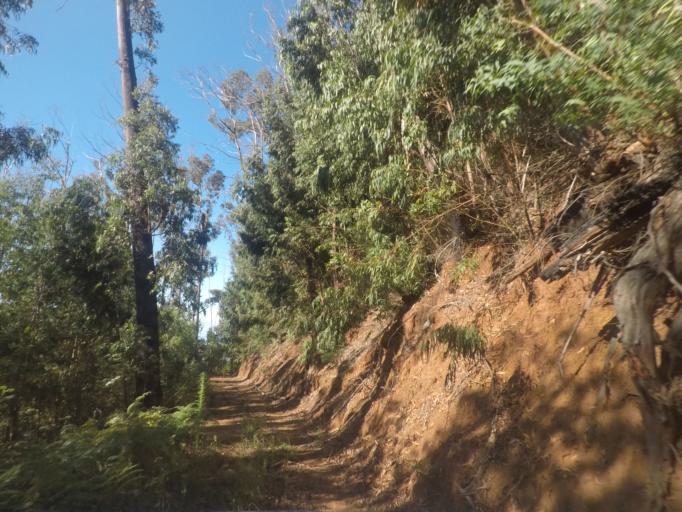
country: PT
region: Madeira
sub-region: Funchal
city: Nossa Senhora do Monte
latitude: 32.6909
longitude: -16.9116
